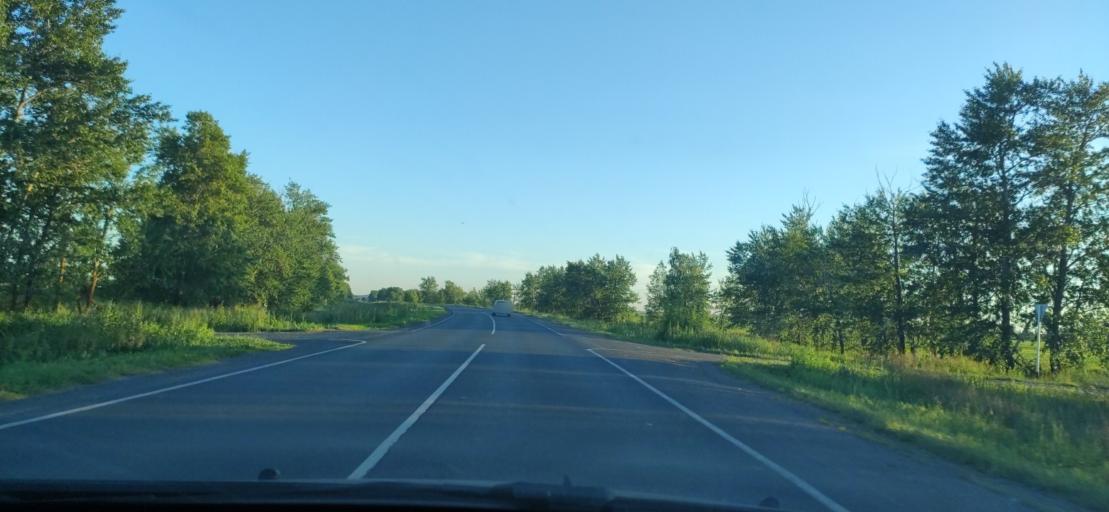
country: RU
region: Ulyanovsk
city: Cherdakly
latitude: 54.3983
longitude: 48.8576
